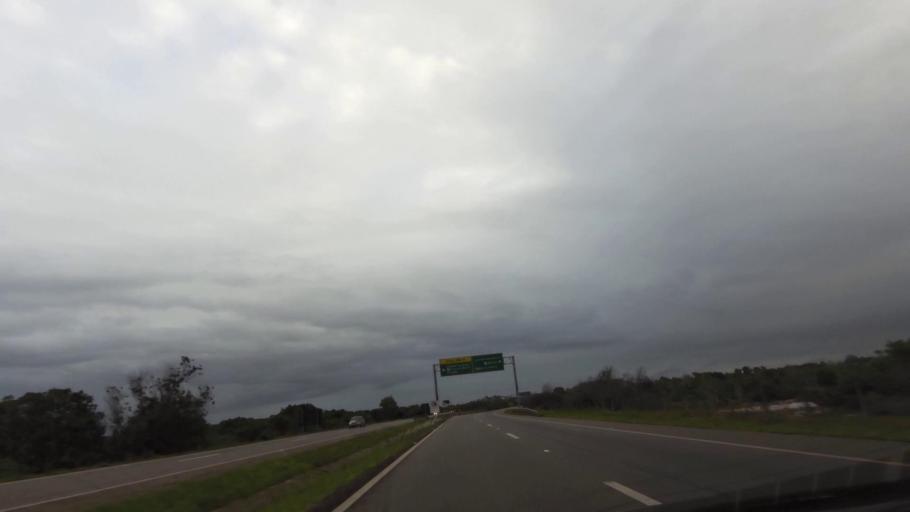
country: BR
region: Espirito Santo
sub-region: Guarapari
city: Guarapari
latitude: -20.6153
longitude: -40.4305
